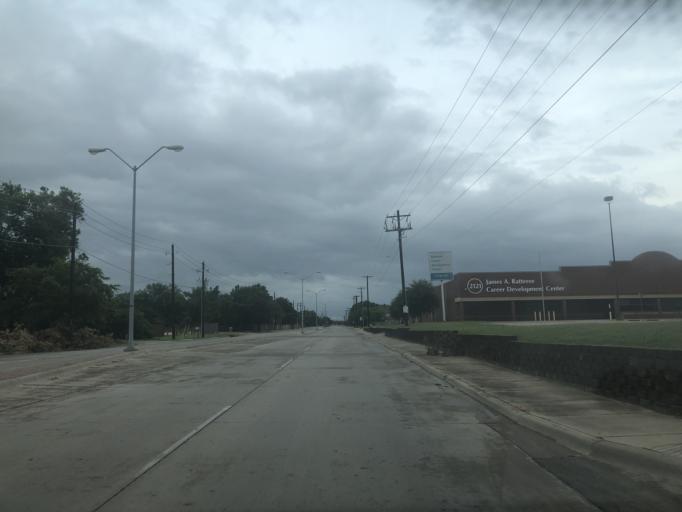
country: US
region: Texas
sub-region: Dallas County
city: Irving
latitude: 32.7933
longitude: -96.9598
